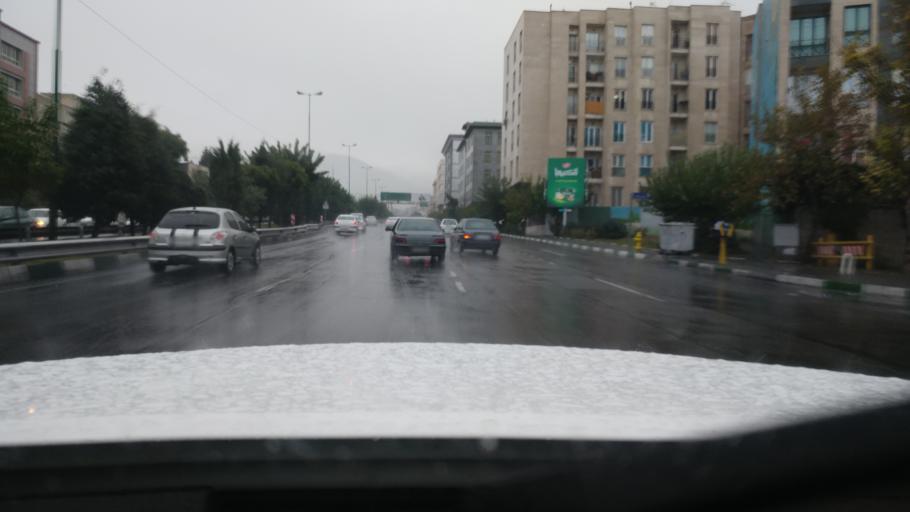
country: IR
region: Tehran
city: Tehran
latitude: 35.7266
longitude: 51.3099
